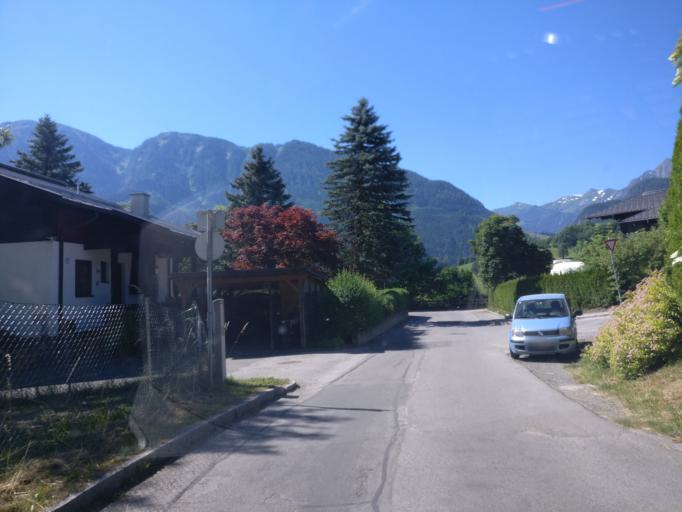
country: AT
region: Salzburg
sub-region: Politischer Bezirk Sankt Johann im Pongau
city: Goldegg
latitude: 47.3161
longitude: 13.0885
